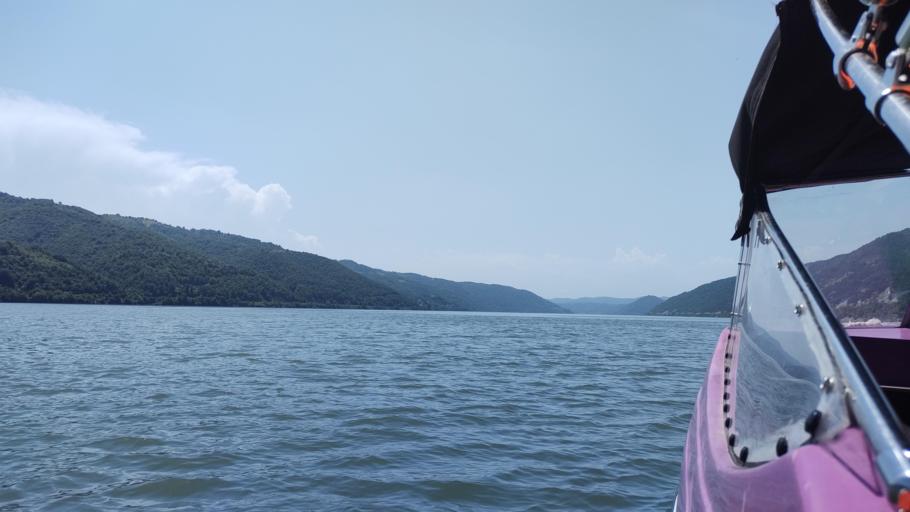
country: RO
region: Mehedinti
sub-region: Comuna Svinita
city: Svinita
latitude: 44.5281
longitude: 22.2062
